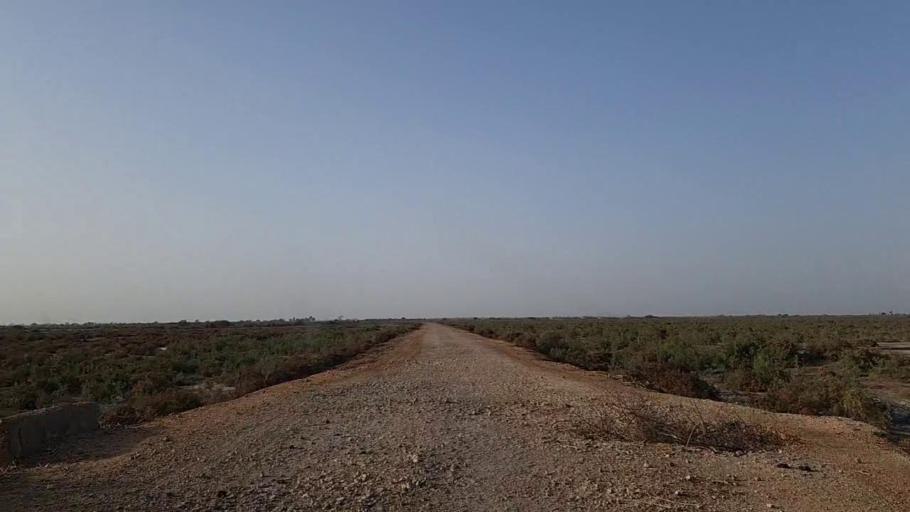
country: PK
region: Sindh
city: Jati
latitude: 24.3586
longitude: 68.1471
